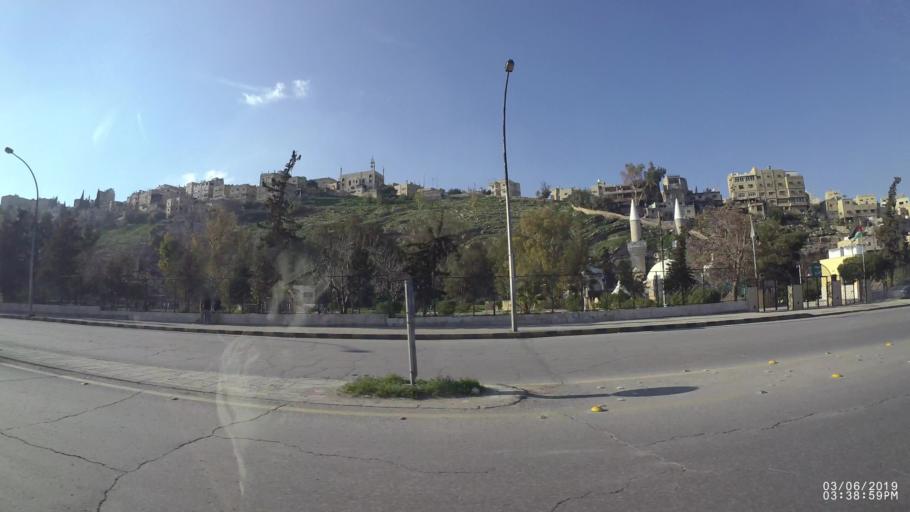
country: JO
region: Amman
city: Amman
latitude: 31.9695
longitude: 35.9668
